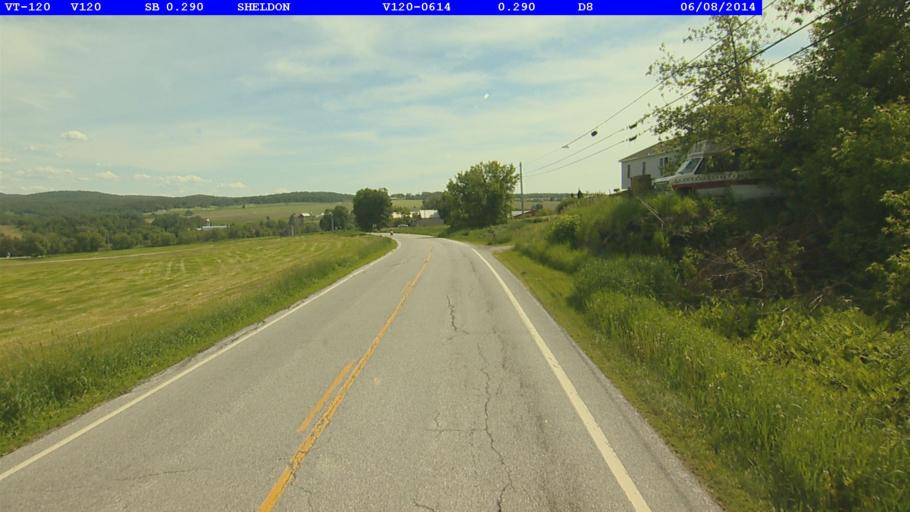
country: US
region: Vermont
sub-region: Franklin County
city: Enosburg Falls
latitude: 44.9145
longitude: -72.9049
